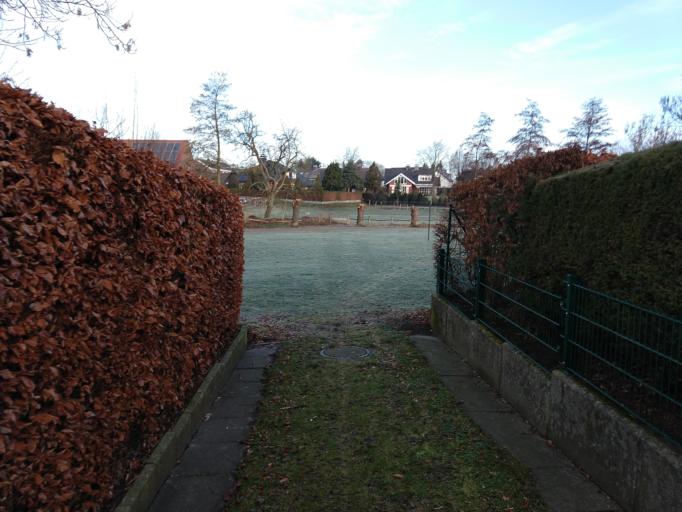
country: DE
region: North Rhine-Westphalia
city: Oelde
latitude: 51.8222
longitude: 8.1334
